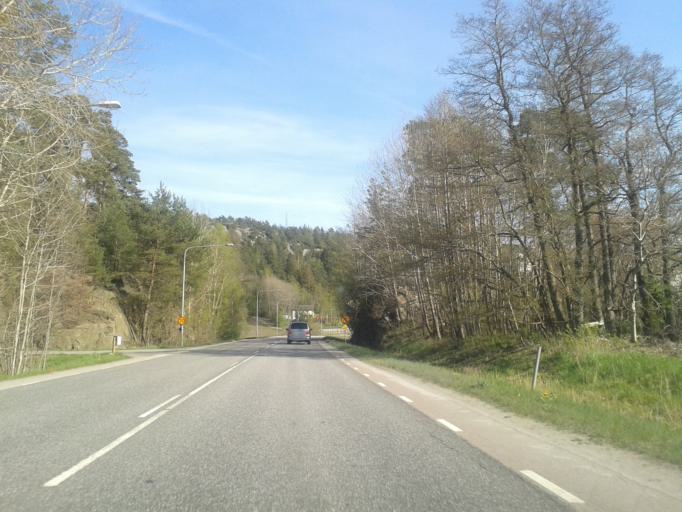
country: SE
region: Vaestra Goetaland
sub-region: Ale Kommun
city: Nodinge-Nol
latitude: 57.8972
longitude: 12.0639
